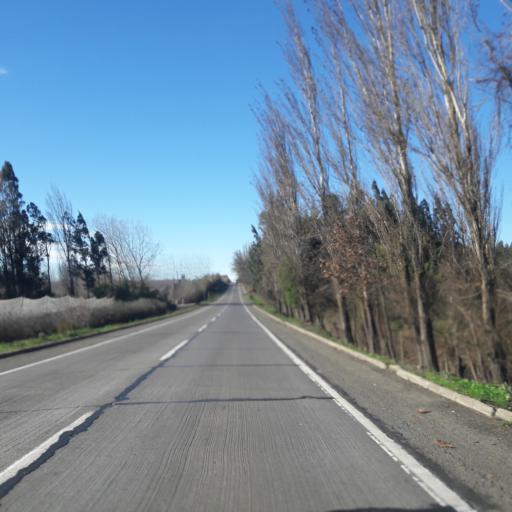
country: CL
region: Araucania
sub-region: Provincia de Malleco
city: Angol
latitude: -37.7499
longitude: -72.5890
